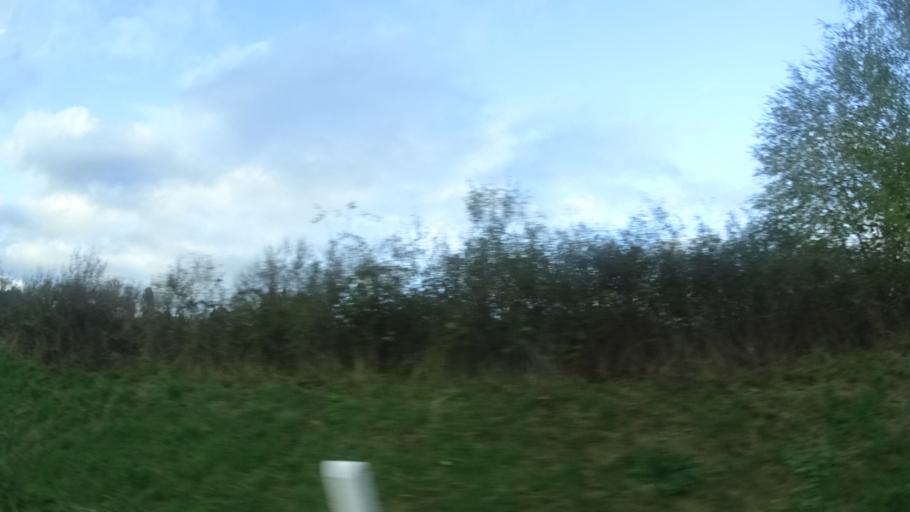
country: DE
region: Hesse
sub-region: Regierungsbezirk Kassel
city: Flieden
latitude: 50.4530
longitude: 9.5634
